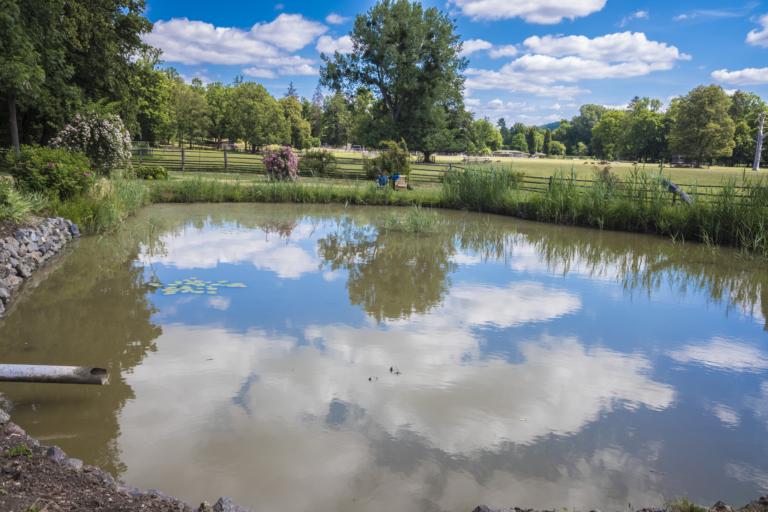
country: DE
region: Bavaria
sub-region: Upper Franconia
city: Weitramsdorf
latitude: 50.2301
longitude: 10.8605
